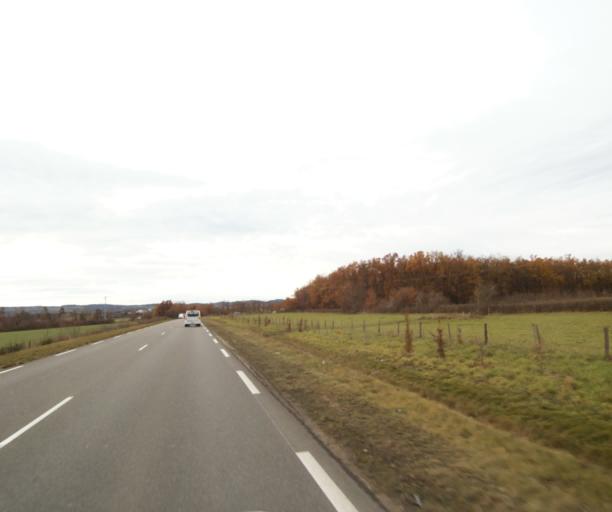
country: FR
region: Rhone-Alpes
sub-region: Departement de la Loire
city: Sury-le-Comtal
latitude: 45.5180
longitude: 4.1904
